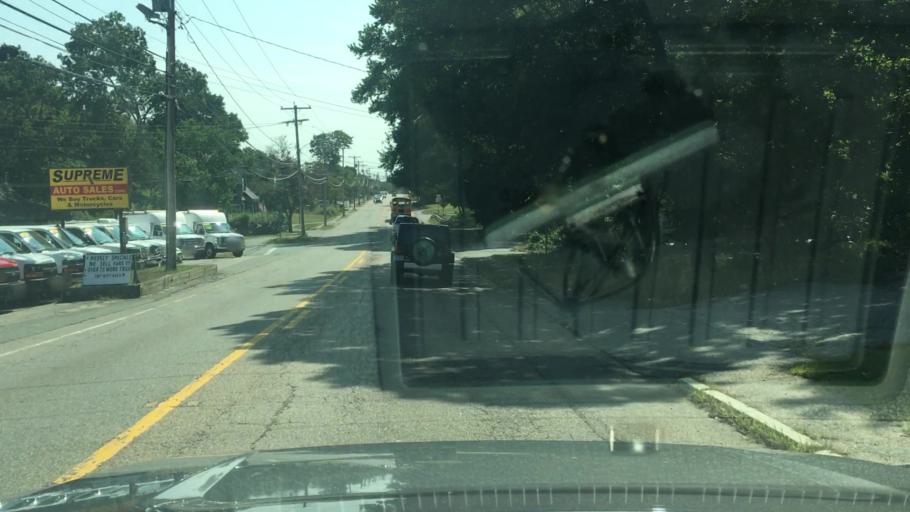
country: US
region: Massachusetts
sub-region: Plymouth County
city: Abington
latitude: 42.1346
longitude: -70.9503
